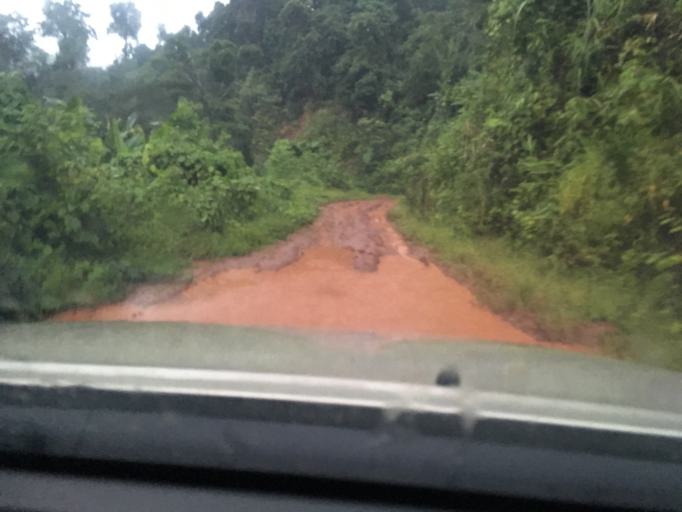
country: LA
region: Oudomxai
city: Muang La
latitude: 21.2452
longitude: 101.9390
